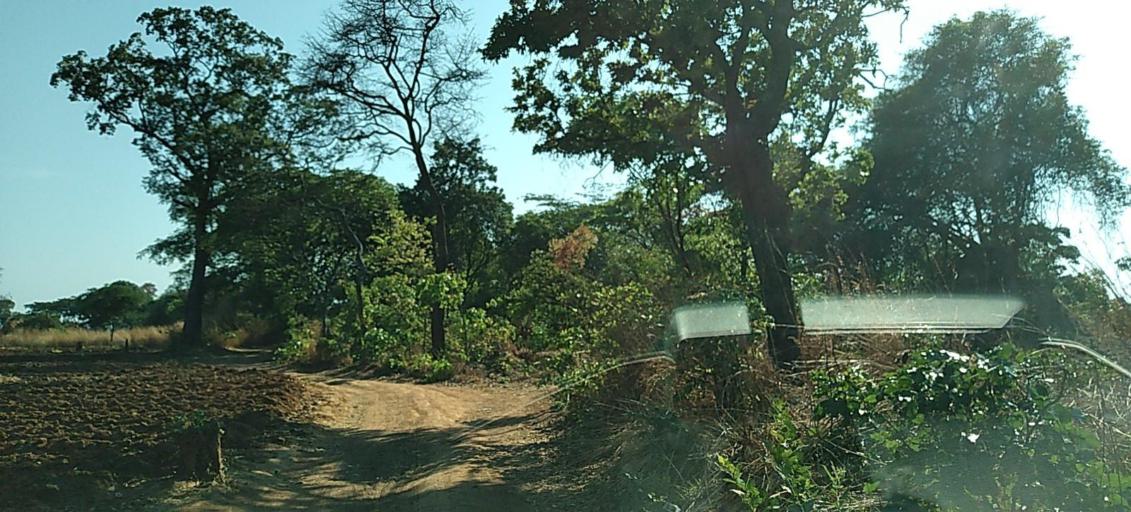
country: ZM
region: Copperbelt
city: Chililabombwe
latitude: -12.3702
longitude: 27.9054
